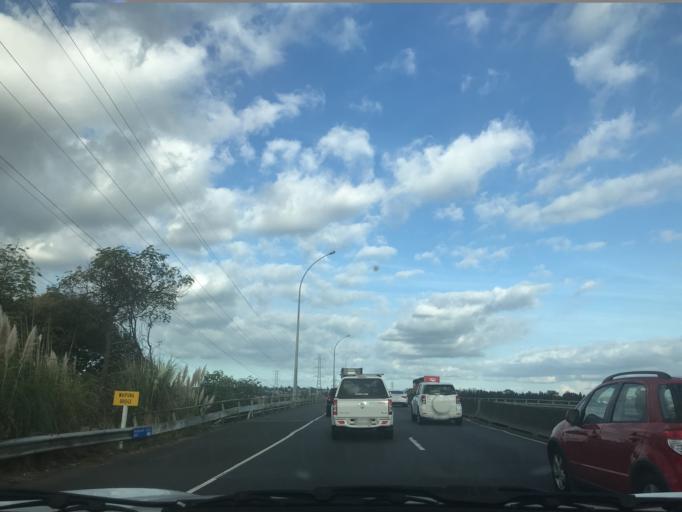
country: NZ
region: Auckland
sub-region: Auckland
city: Tamaki
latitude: -36.9111
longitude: 174.8557
